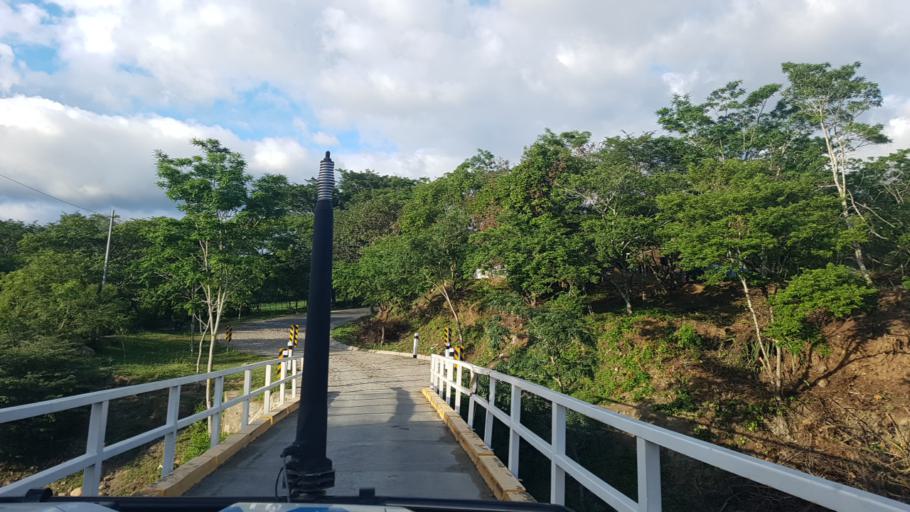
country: NI
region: Nueva Segovia
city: Ocotal
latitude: 13.6415
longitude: -86.5904
